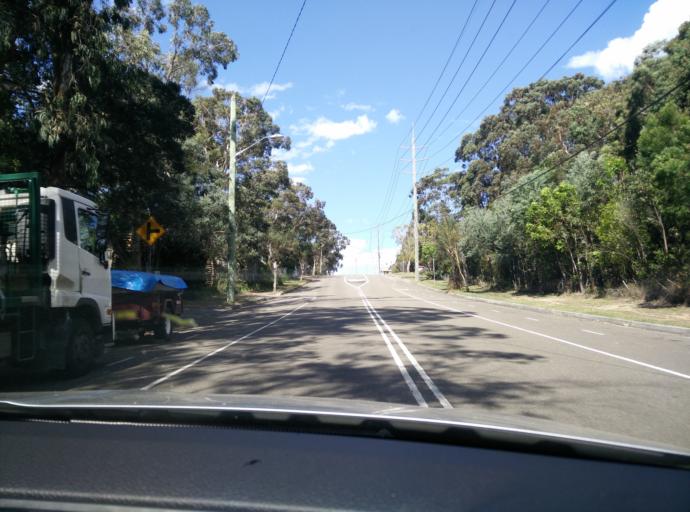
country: AU
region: New South Wales
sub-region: Warringah
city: Allambie Heights
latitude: -33.7552
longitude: 151.2377
